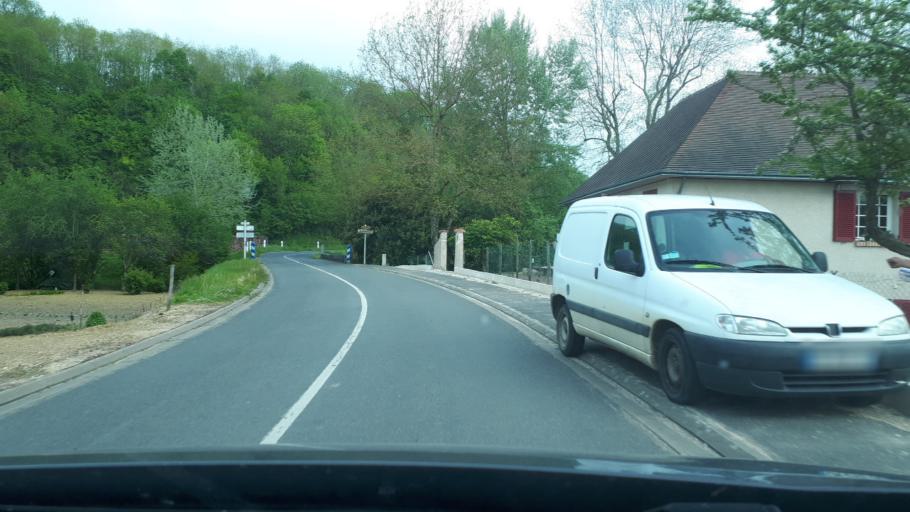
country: FR
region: Centre
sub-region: Departement du Loir-et-Cher
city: Lunay
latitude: 47.8208
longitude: 0.9483
